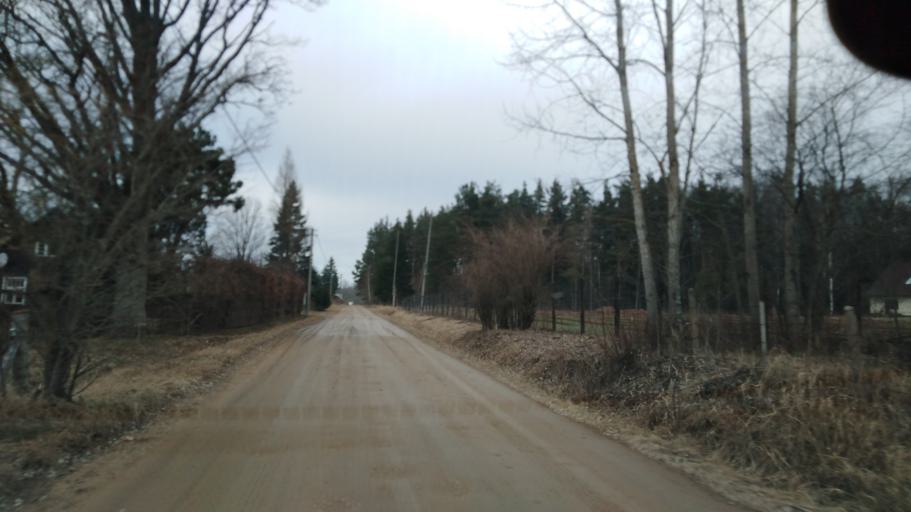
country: LV
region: Kuldigas Rajons
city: Kuldiga
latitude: 56.9855
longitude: 21.9707
